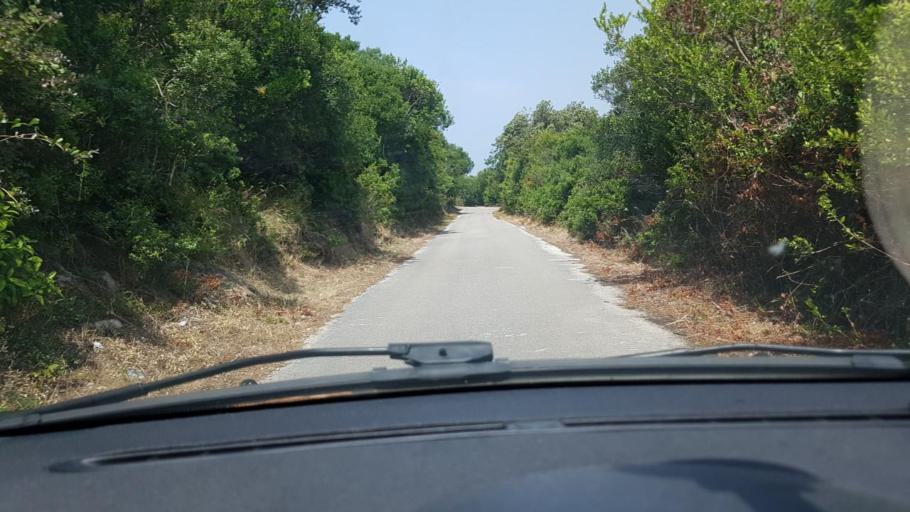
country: ME
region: Herceg Novi
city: Herceg-Novi
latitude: 42.4016
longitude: 18.5176
